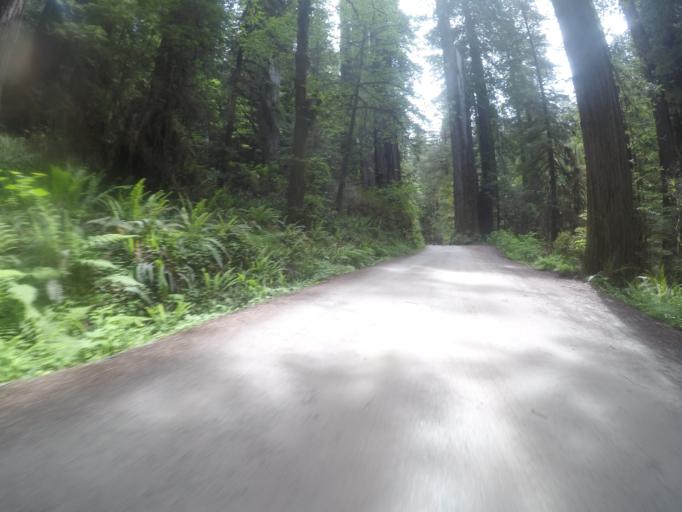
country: US
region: California
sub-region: Del Norte County
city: Bertsch-Oceanview
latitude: 41.7646
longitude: -124.1273
